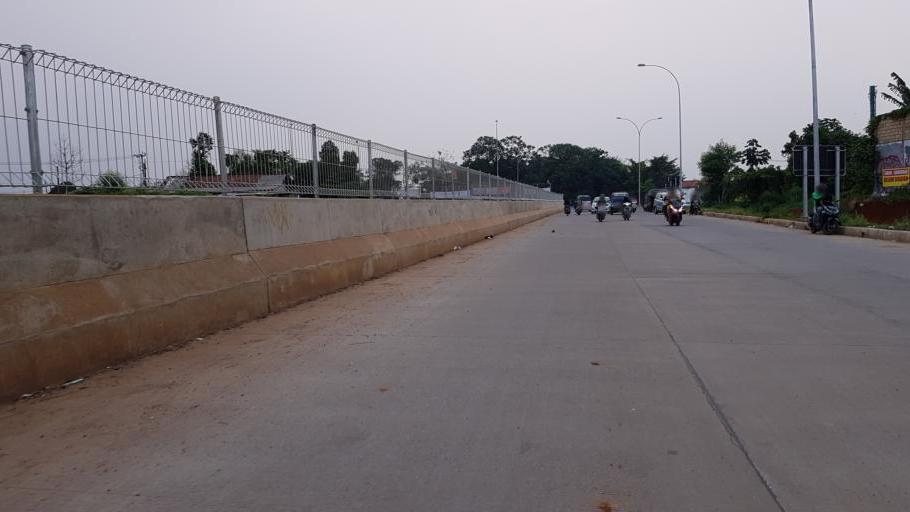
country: ID
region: West Java
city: Depok
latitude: -6.3695
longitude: 106.8145
